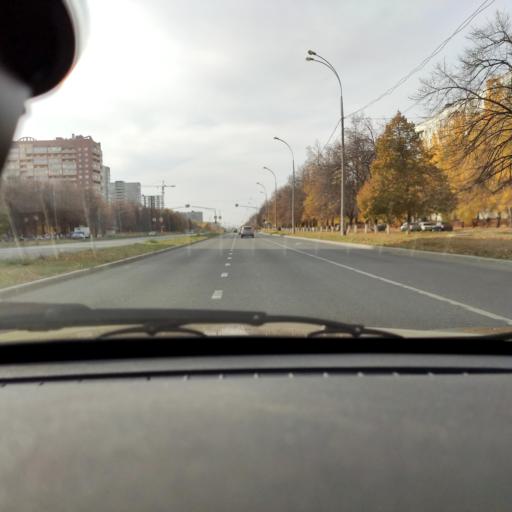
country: RU
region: Samara
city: Tol'yatti
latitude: 53.5268
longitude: 49.3079
